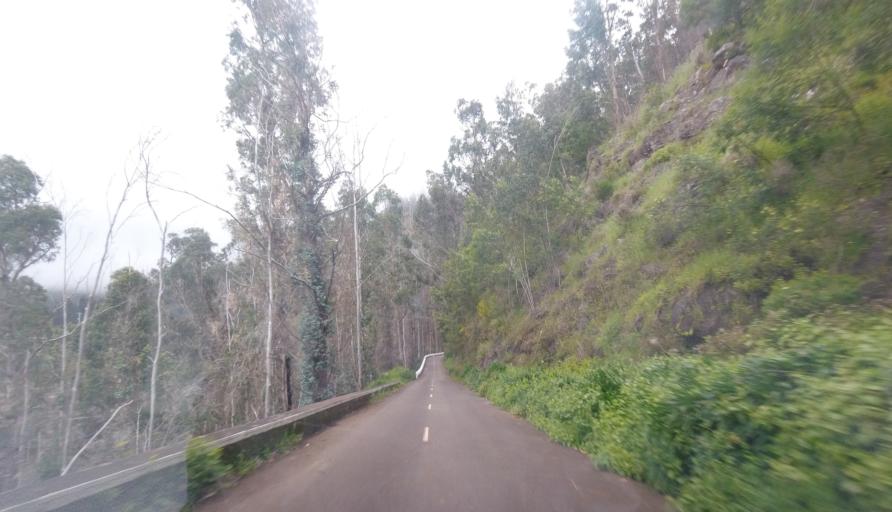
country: PT
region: Madeira
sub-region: Funchal
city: Nossa Senhora do Monte
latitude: 32.6882
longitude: -16.8896
